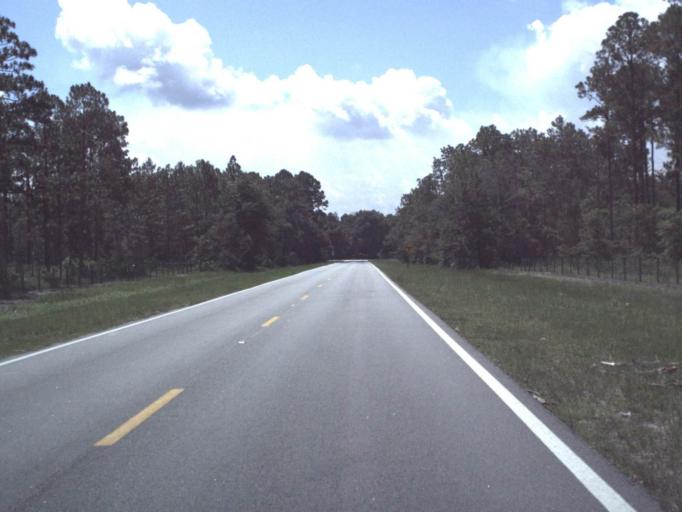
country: US
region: Florida
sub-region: Bradford County
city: Starke
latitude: 29.9835
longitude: -82.0158
